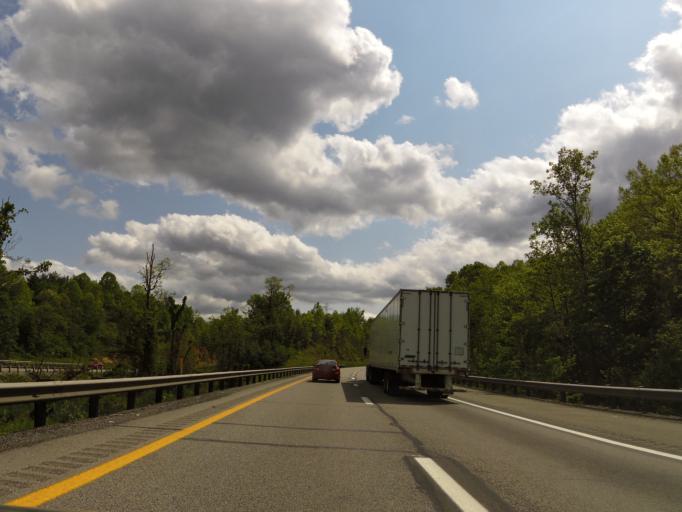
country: US
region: West Virginia
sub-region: Raleigh County
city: Bradley
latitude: 37.9306
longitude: -81.2625
